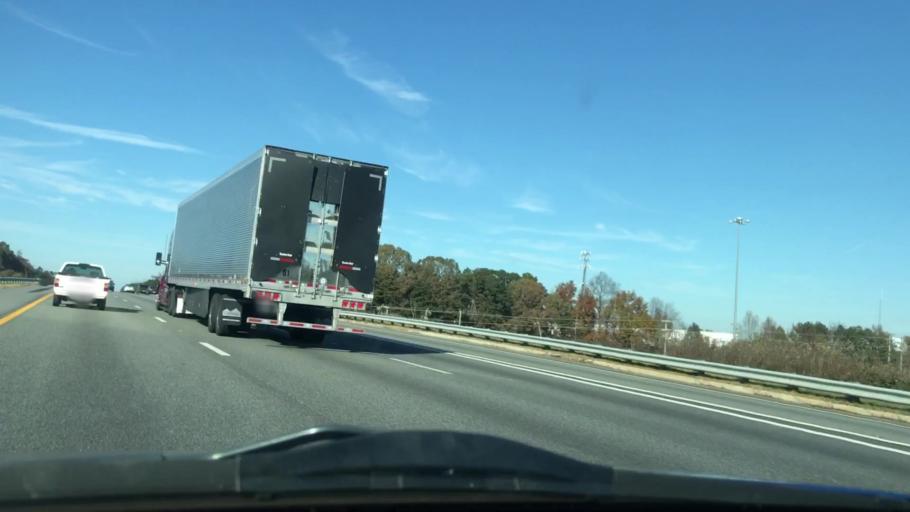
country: US
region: North Carolina
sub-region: Guilford County
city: High Point
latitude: 35.9652
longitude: -79.9747
